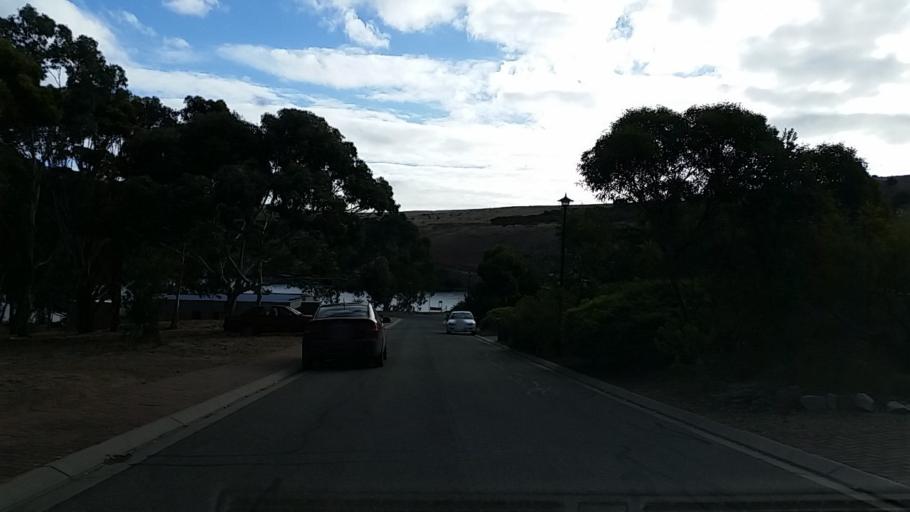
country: AU
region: South Australia
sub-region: Yankalilla
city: Normanville
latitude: -35.5056
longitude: 138.2453
